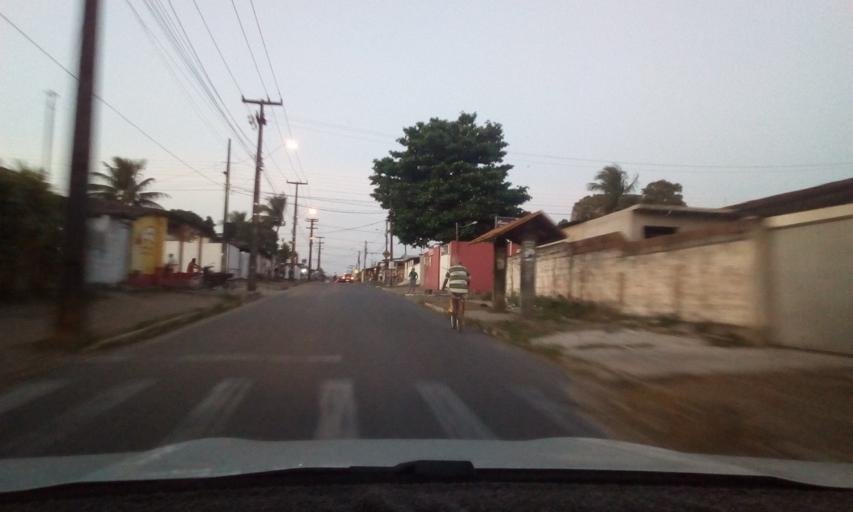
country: BR
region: Paraiba
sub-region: Bayeux
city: Bayeux
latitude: -7.1662
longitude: -34.9087
